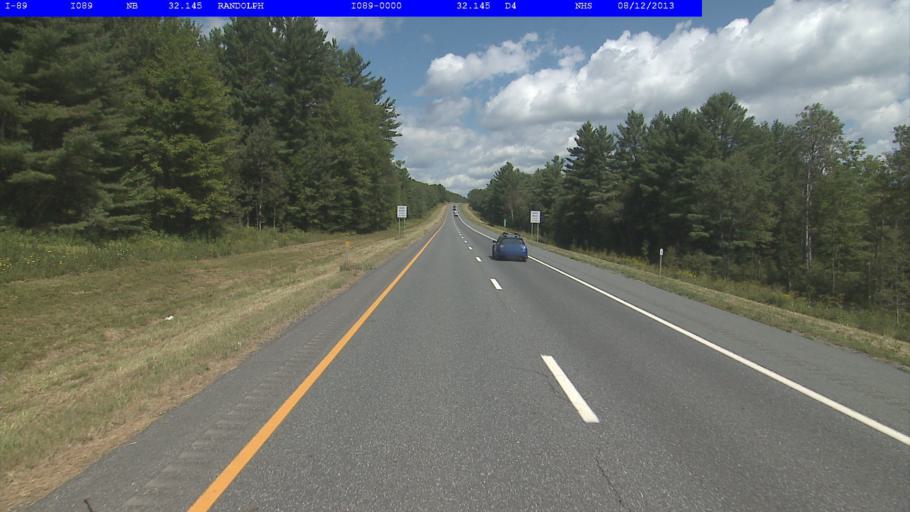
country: US
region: Vermont
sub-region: Orange County
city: Randolph
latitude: 43.9624
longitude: -72.6236
